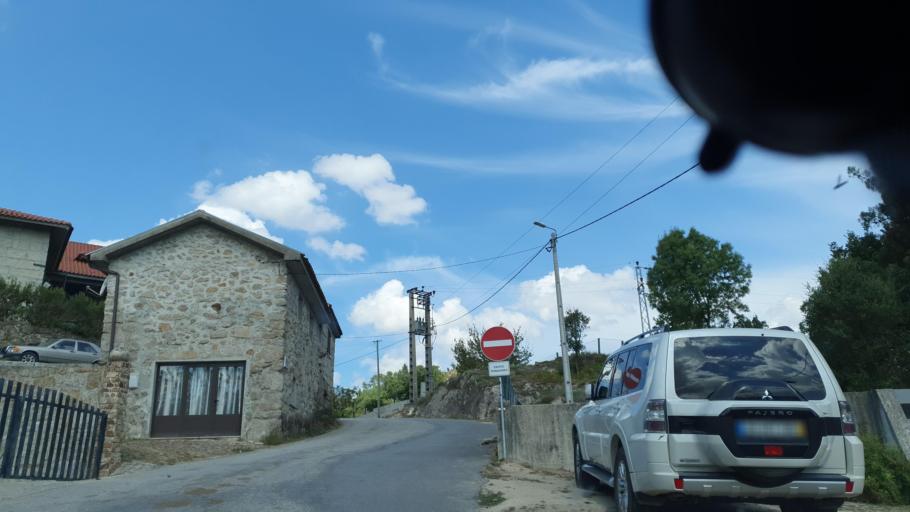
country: PT
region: Braga
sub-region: Vieira do Minho
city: Vieira do Minho
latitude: 41.7068
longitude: -8.0509
